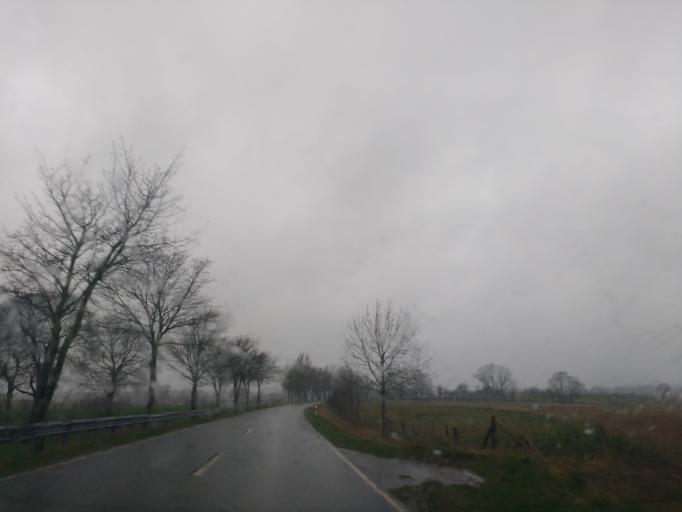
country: DE
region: Schleswig-Holstein
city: Blekendorf
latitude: 54.2979
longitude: 10.6650
